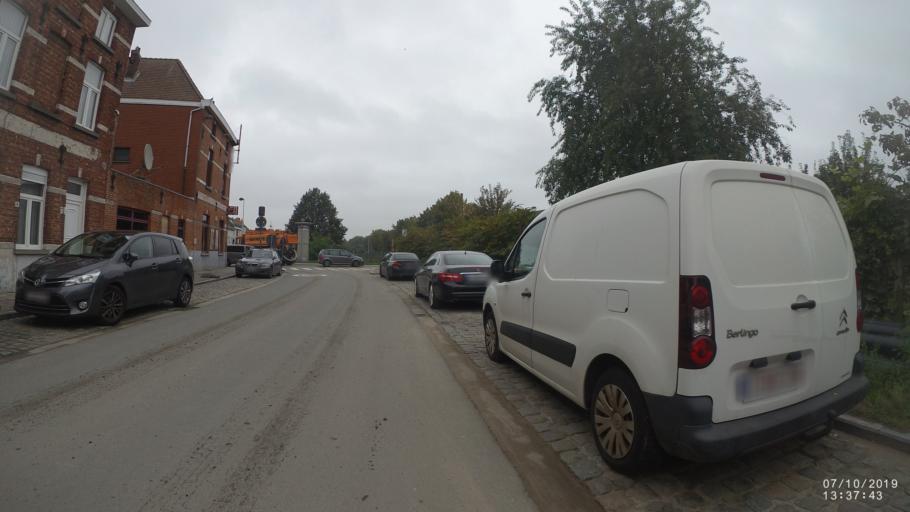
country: BE
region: Flanders
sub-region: Provincie Oost-Vlaanderen
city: Gent
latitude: 51.0735
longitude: 3.7304
